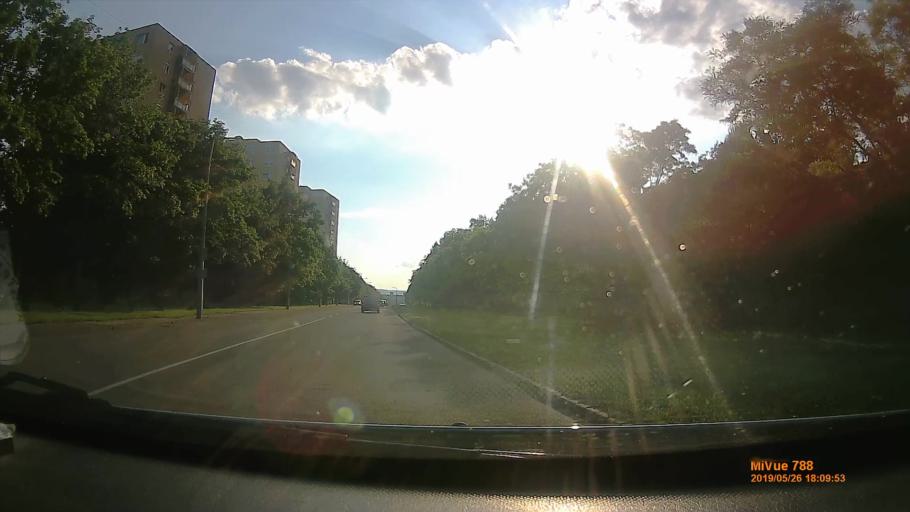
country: HU
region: Borsod-Abauj-Zemplen
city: Miskolc
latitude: 48.1058
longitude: 20.7679
